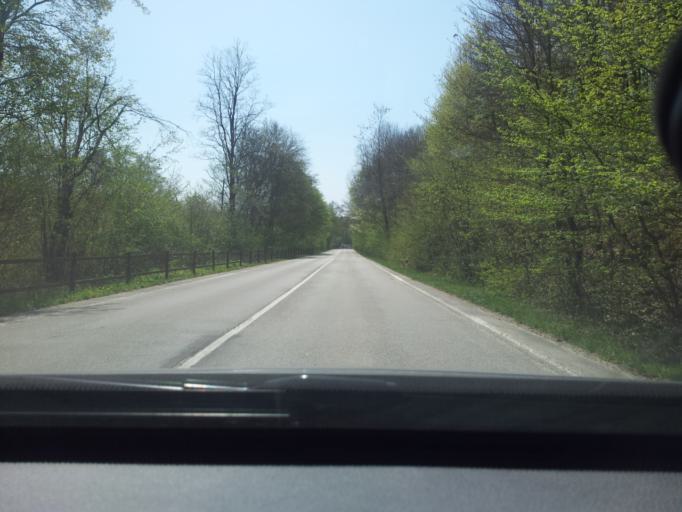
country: SK
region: Nitriansky
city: Zlate Moravce
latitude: 48.4560
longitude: 18.4108
